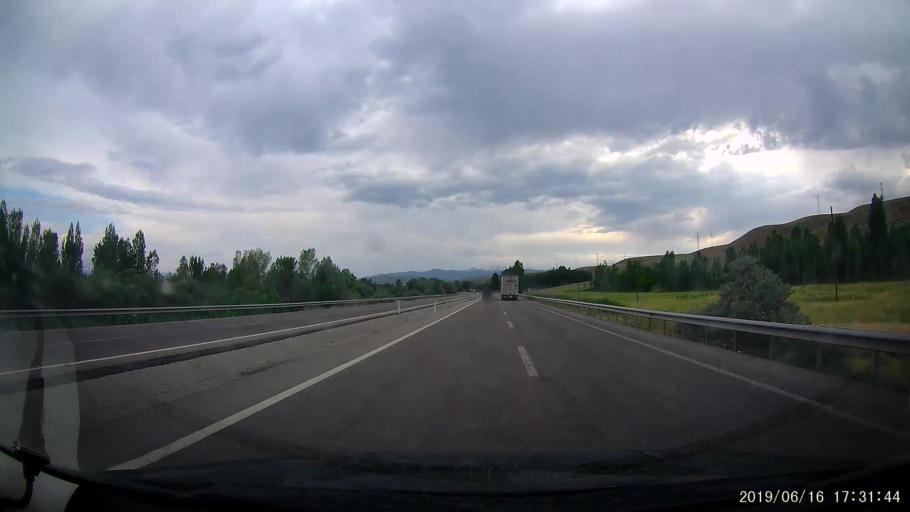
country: TR
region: Erzincan
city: Tercan
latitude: 39.7721
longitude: 40.3157
